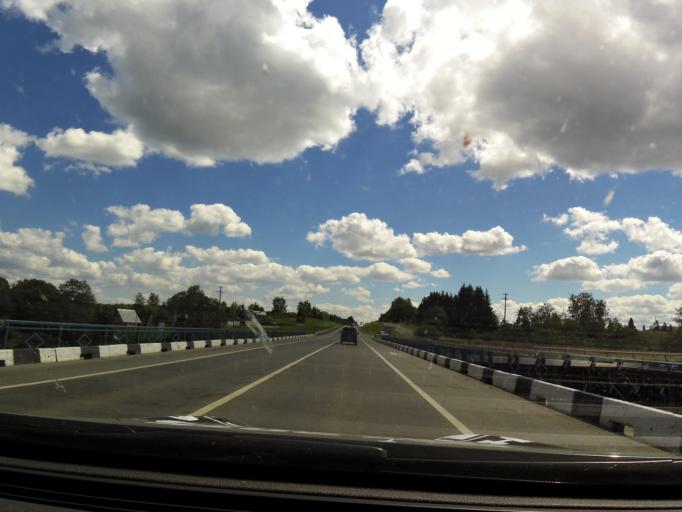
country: RU
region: Vologda
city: Molochnoye
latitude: 59.2809
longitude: 39.7060
